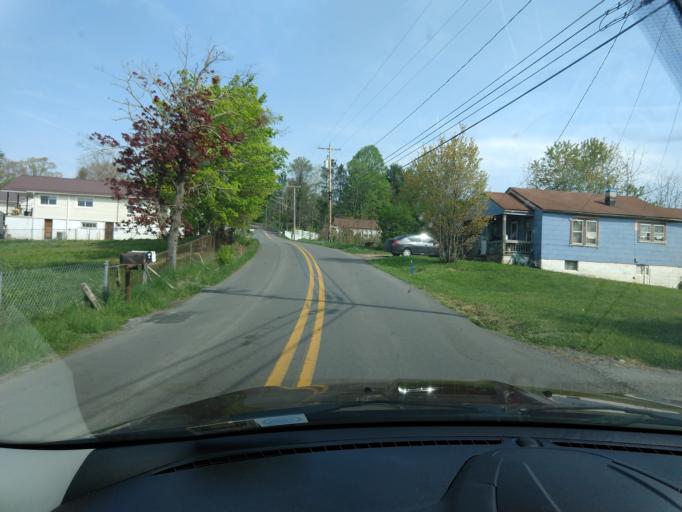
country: US
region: West Virginia
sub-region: Raleigh County
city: Crab Orchard
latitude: 37.7448
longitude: -81.2311
